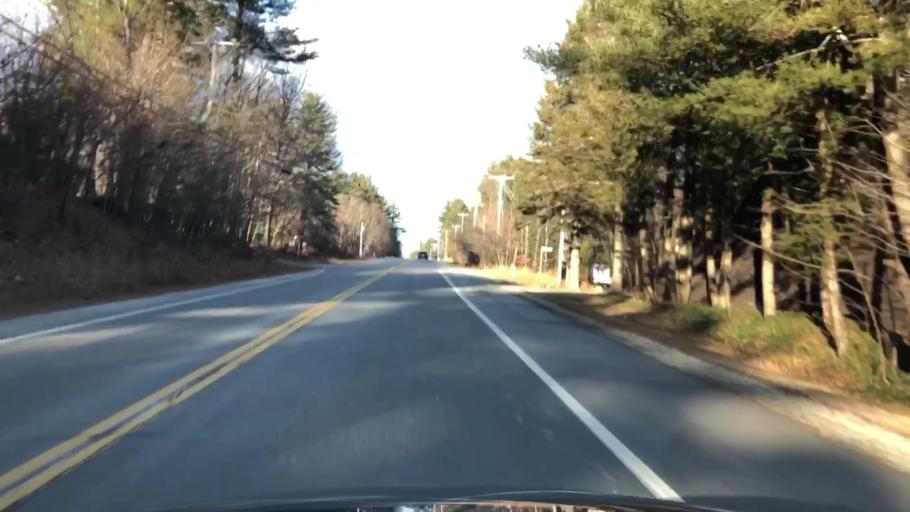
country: US
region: New Hampshire
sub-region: Hillsborough County
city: Milford
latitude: 42.7896
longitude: -71.6582
